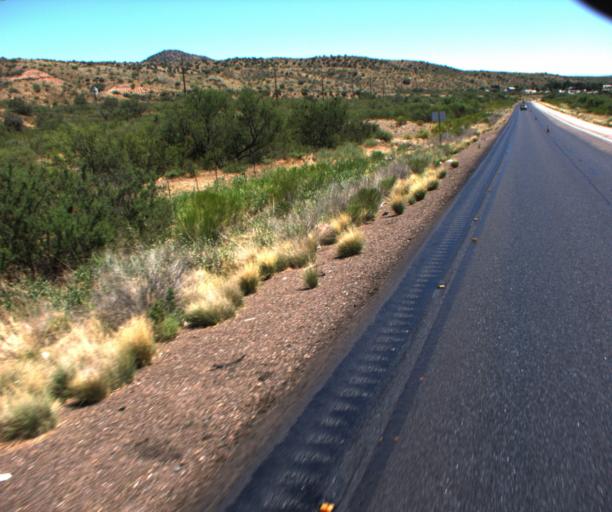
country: US
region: Arizona
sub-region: Gila County
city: Payson
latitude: 34.1162
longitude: -111.3563
